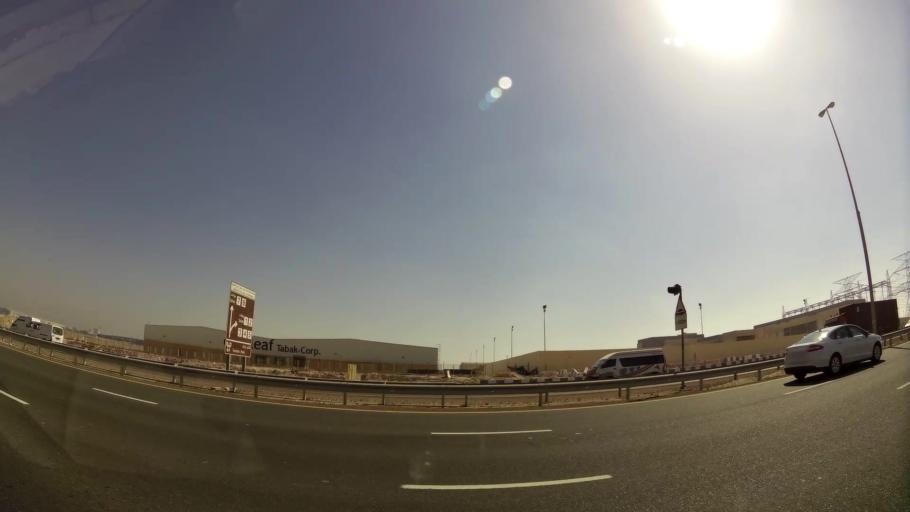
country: AE
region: Dubai
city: Dubai
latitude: 24.9406
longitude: 55.0701
